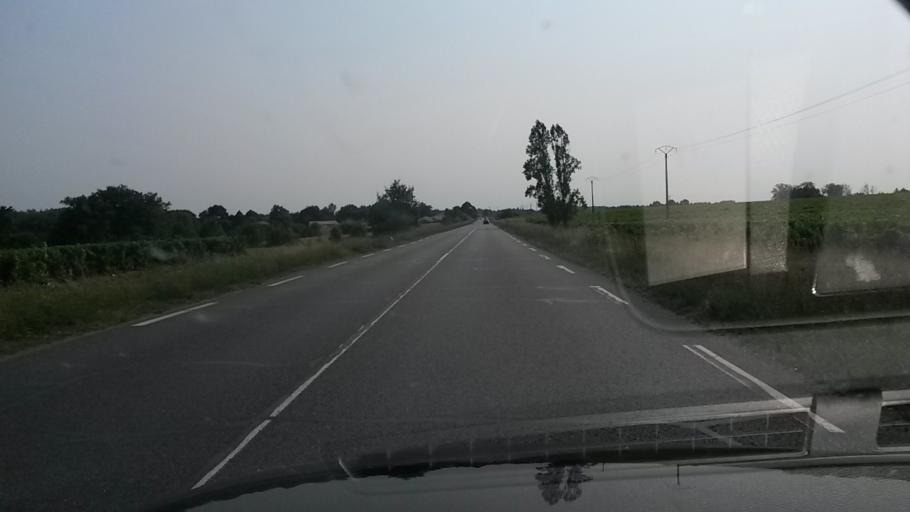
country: FR
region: Pays de la Loire
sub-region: Departement de la Loire-Atlantique
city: Mouzillon
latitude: 47.1515
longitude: -1.2790
